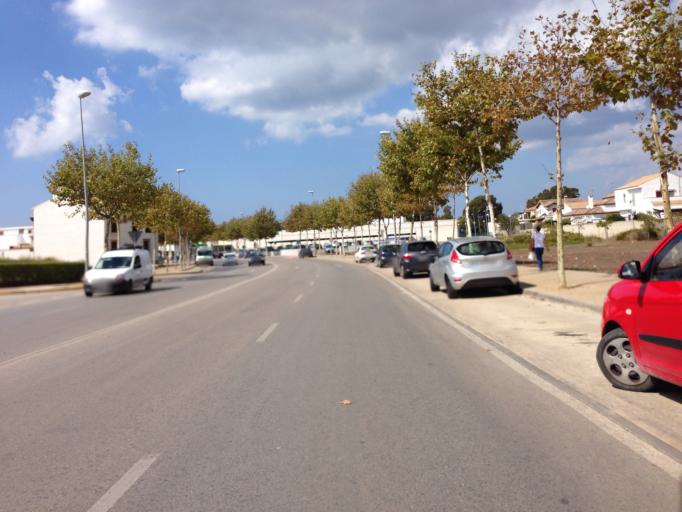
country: ES
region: Andalusia
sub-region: Provincia de Cadiz
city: Conil de la Frontera
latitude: 36.2845
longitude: -6.0863
